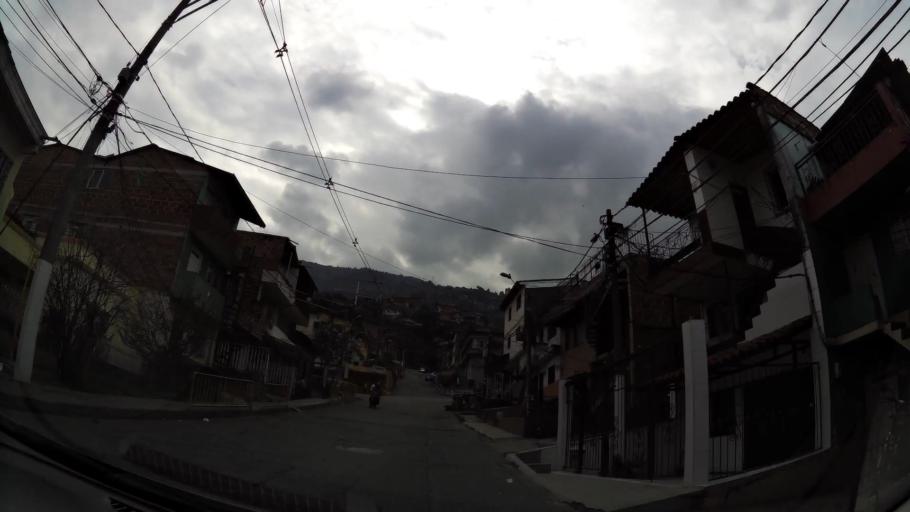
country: CO
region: Antioquia
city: Medellin
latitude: 6.2834
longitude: -75.5495
